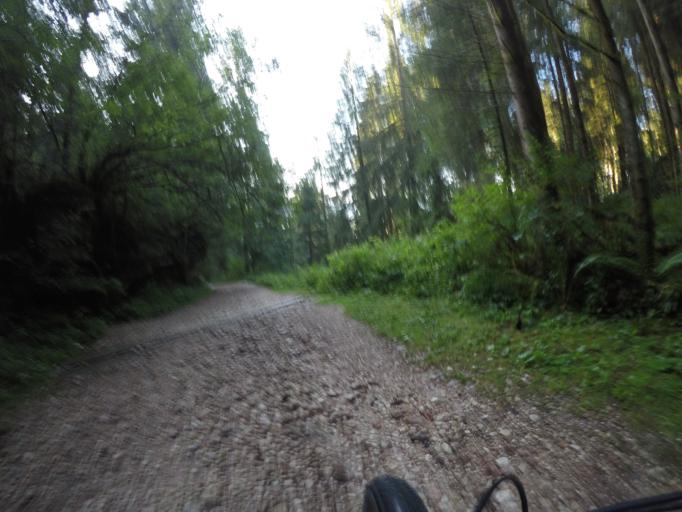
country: IT
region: Veneto
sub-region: Provincia di Vicenza
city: Asiago
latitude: 45.8545
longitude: 11.5139
